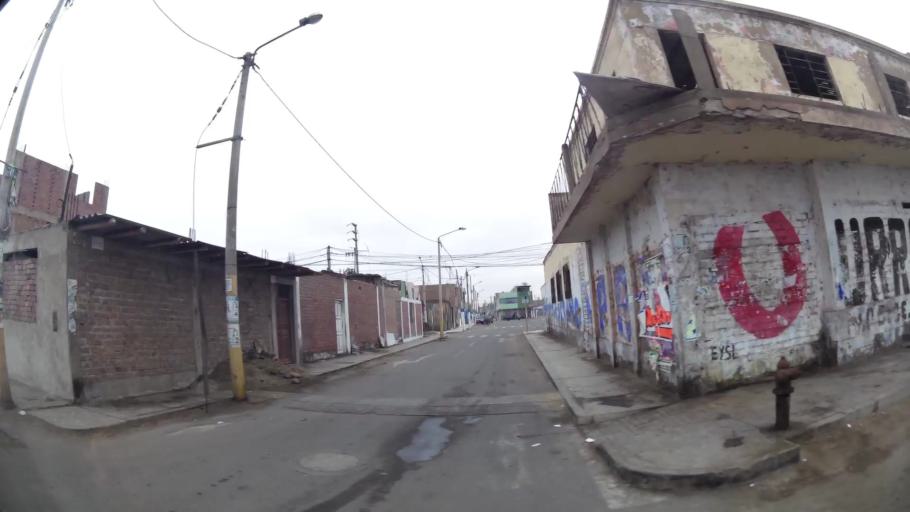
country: PE
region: Ica
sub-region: Provincia de Pisco
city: Pisco
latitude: -13.7310
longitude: -76.2236
